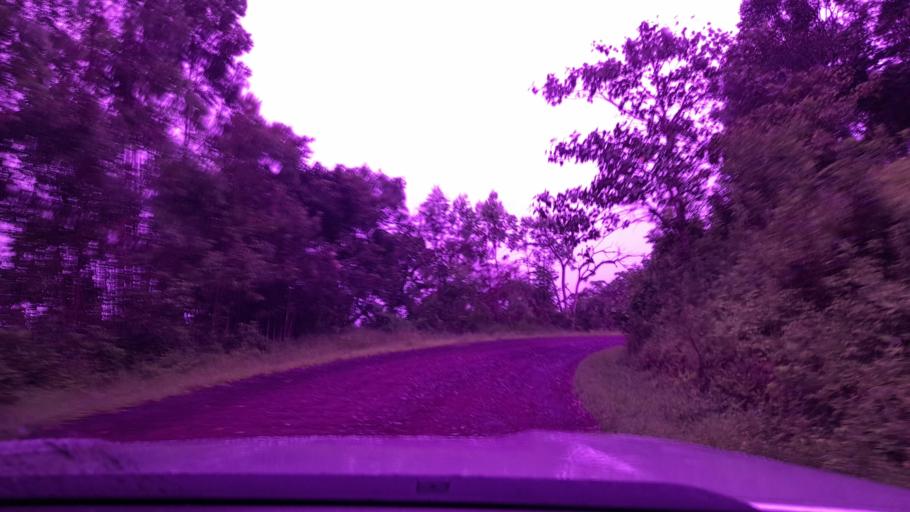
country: ET
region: Oromiya
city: Metu
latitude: 8.4506
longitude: 35.6313
